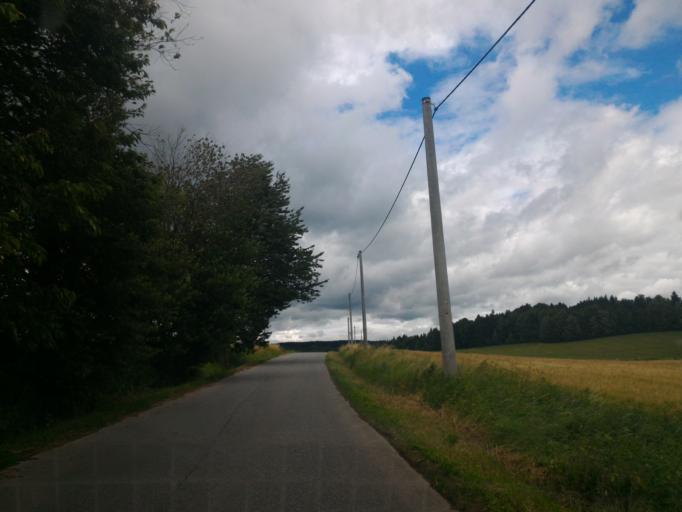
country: CZ
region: Vysocina
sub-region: Okres Jihlava
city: Telc
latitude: 49.2405
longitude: 15.4322
